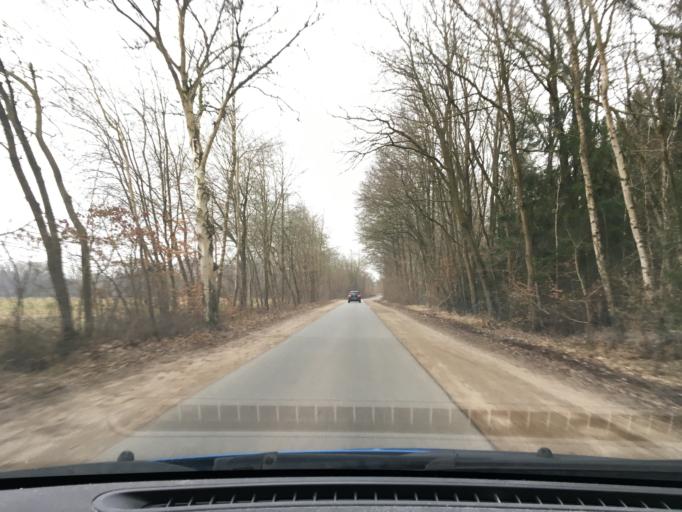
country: DE
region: Lower Saxony
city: Vogelsen
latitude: 53.2850
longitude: 10.3456
